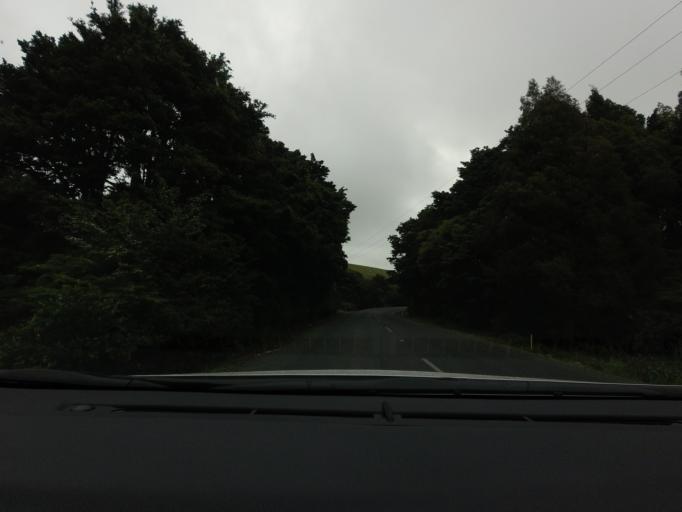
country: NZ
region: Auckland
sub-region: Auckland
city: Wellsford
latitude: -36.2790
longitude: 174.5858
